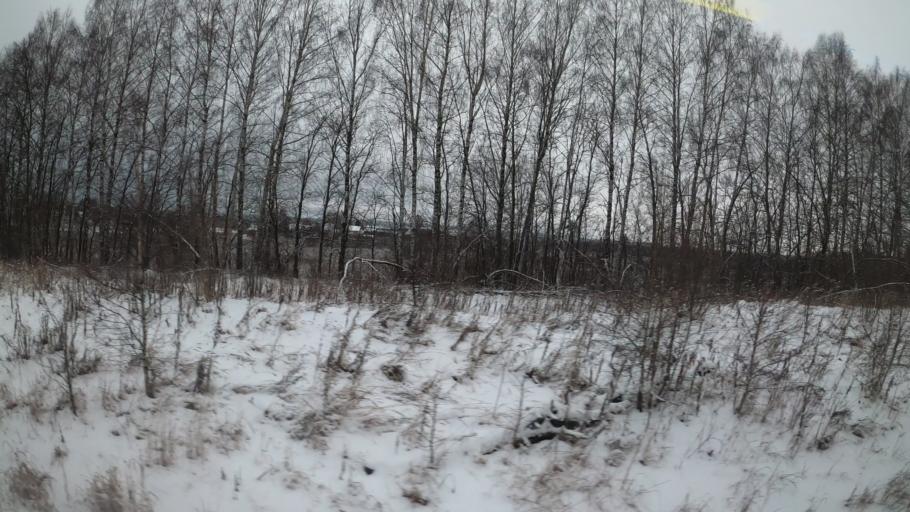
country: RU
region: Jaroslavl
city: Pereslavl'-Zalesskiy
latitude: 56.6854
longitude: 38.9200
